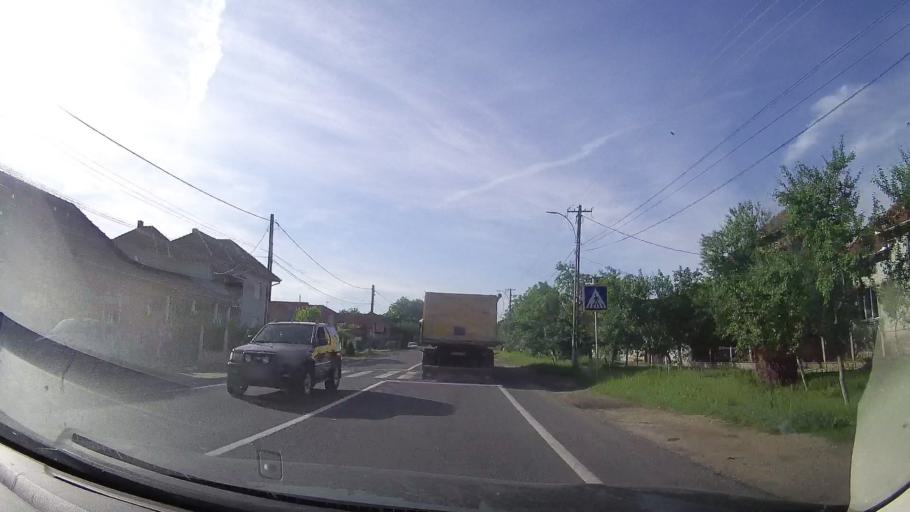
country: RO
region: Timis
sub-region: Comuna Costeiu
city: Costeiu
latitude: 45.7297
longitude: 21.8686
